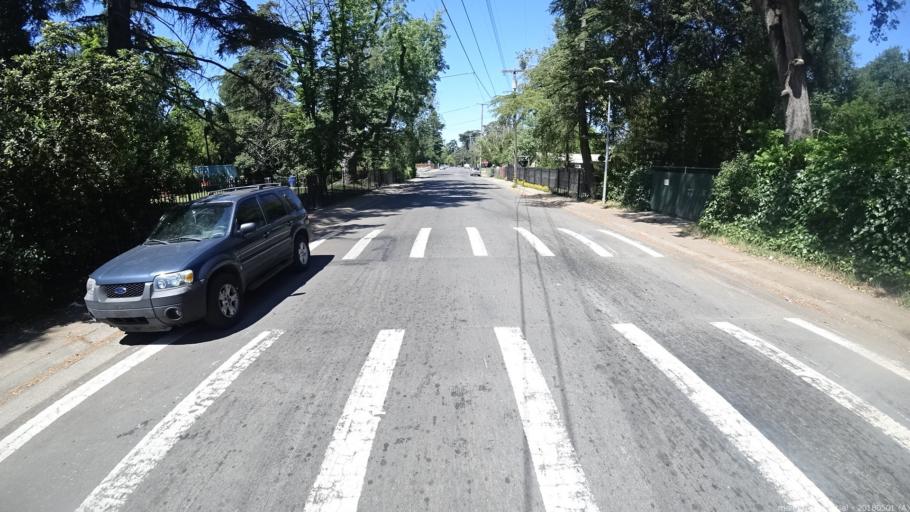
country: US
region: California
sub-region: Sacramento County
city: Arden-Arcade
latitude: 38.6301
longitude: -121.4340
